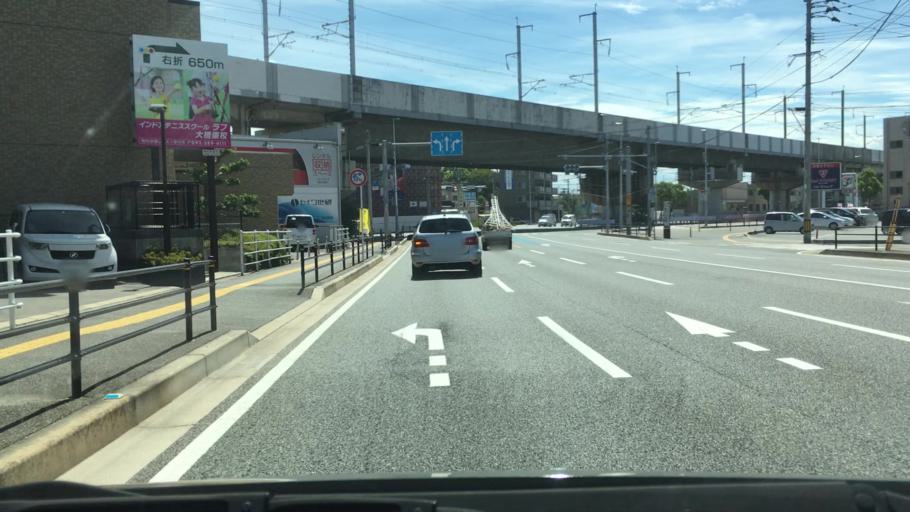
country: JP
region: Fukuoka
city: Fukuoka-shi
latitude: 33.5618
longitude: 130.4350
